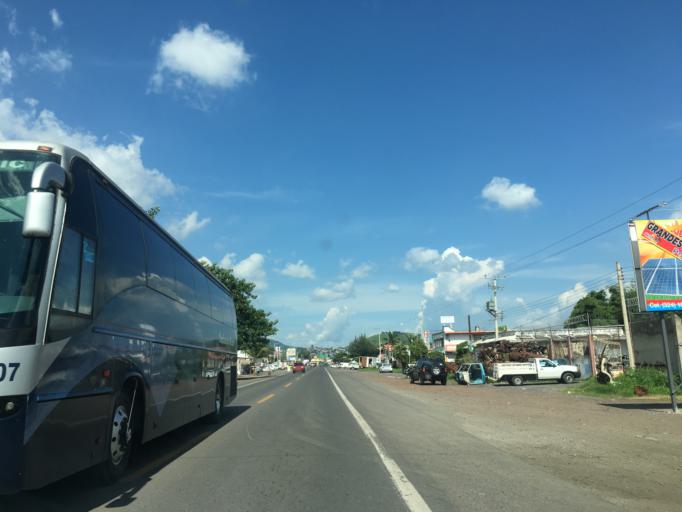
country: MX
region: Nayarit
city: Ixtlan del Rio
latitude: 21.0374
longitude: -104.3870
